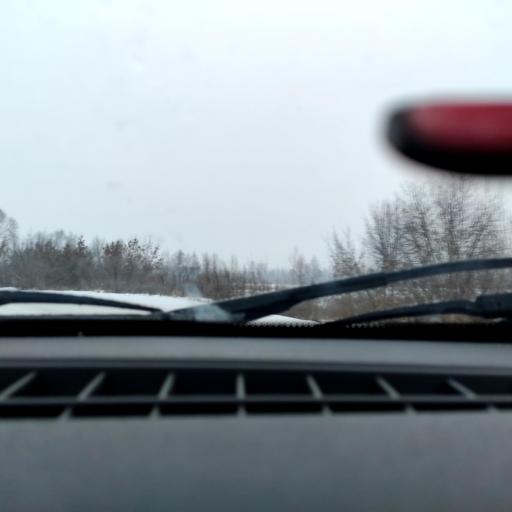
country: RU
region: Bashkortostan
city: Blagoveshchensk
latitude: 54.9033
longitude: 56.0121
